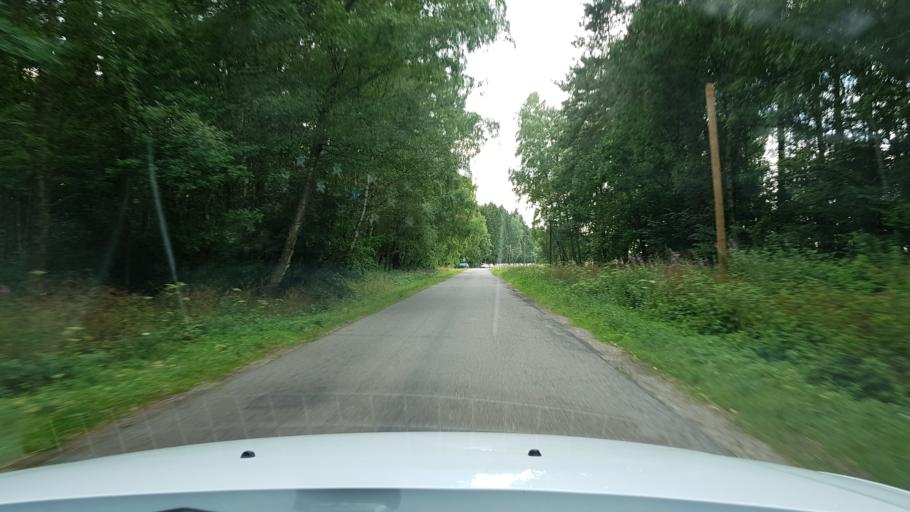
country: PL
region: West Pomeranian Voivodeship
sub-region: Powiat drawski
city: Wierzchowo
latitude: 53.4542
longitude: 16.1166
